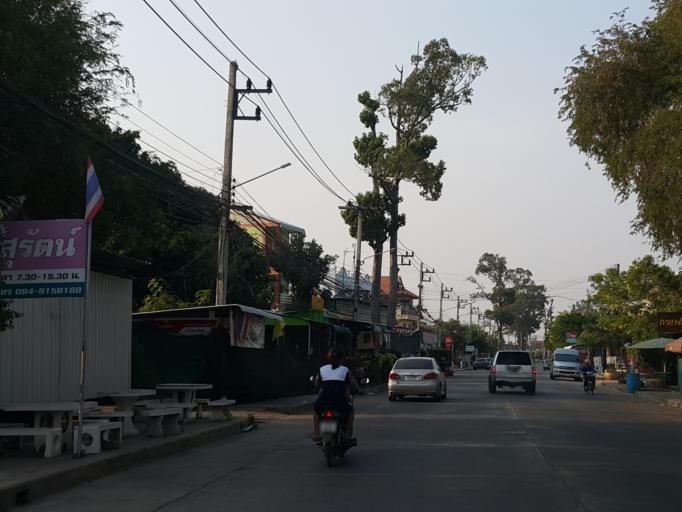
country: TH
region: Chai Nat
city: Sankhaburi
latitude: 15.0513
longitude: 100.1605
